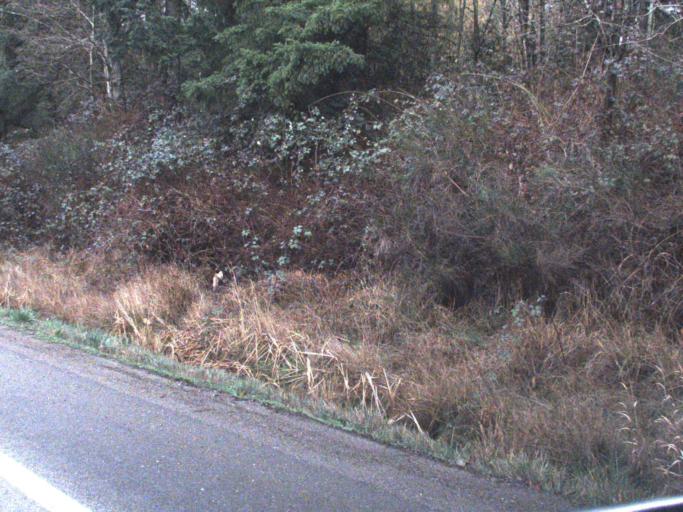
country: US
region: Washington
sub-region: Snohomish County
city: Lake Stevens
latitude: 48.0298
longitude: -122.0853
